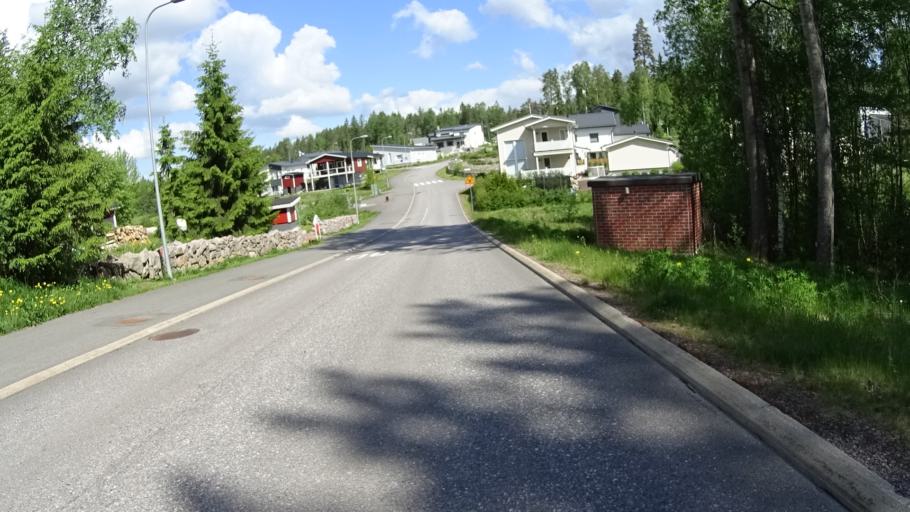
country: FI
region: Uusimaa
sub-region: Helsinki
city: Espoo
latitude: 60.2273
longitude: 24.6390
